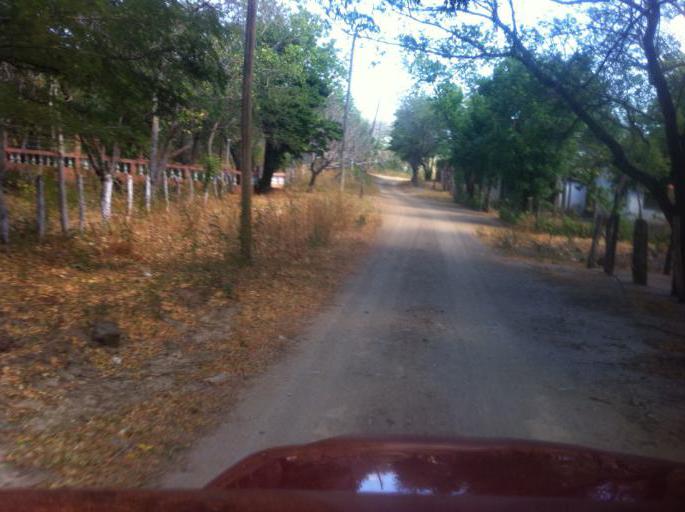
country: NI
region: Carazo
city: Santa Teresa
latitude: 11.6072
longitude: -86.3032
